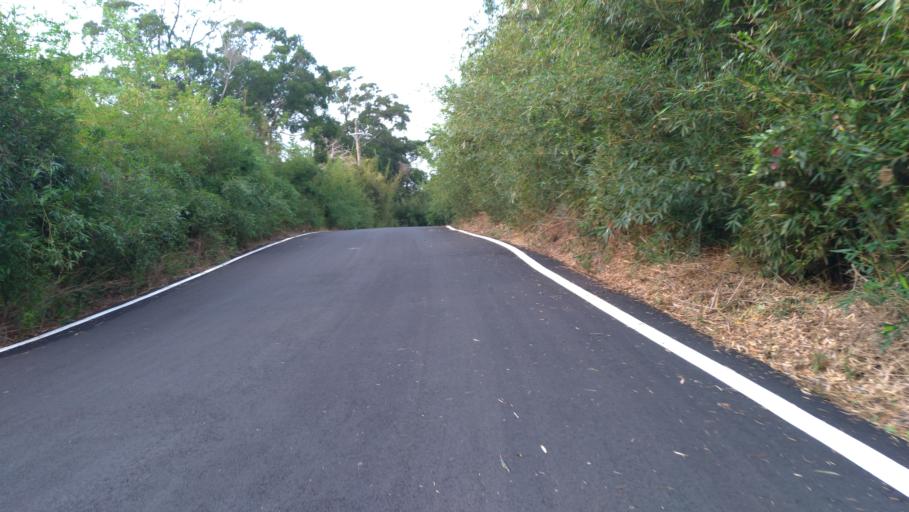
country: TW
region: Taiwan
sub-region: Hsinchu
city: Hsinchu
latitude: 24.7514
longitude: 120.9886
